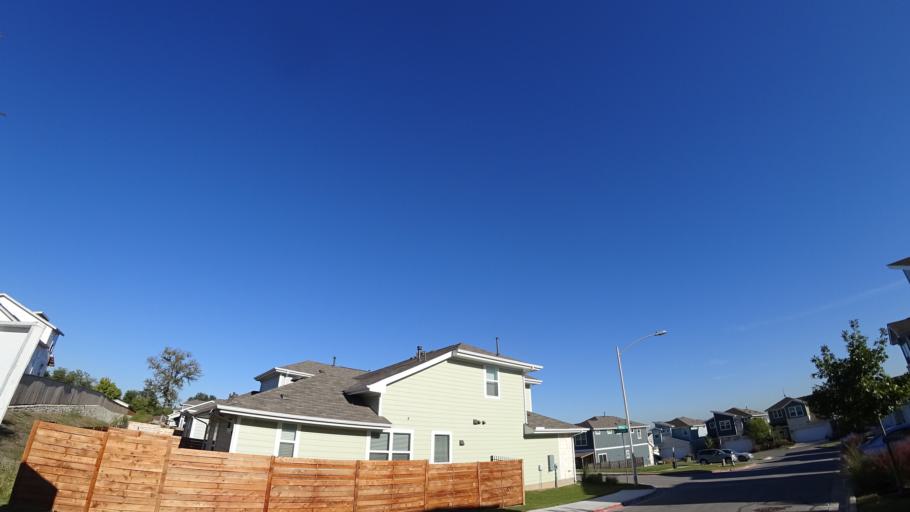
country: US
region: Texas
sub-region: Travis County
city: Austin
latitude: 30.2183
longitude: -97.6987
